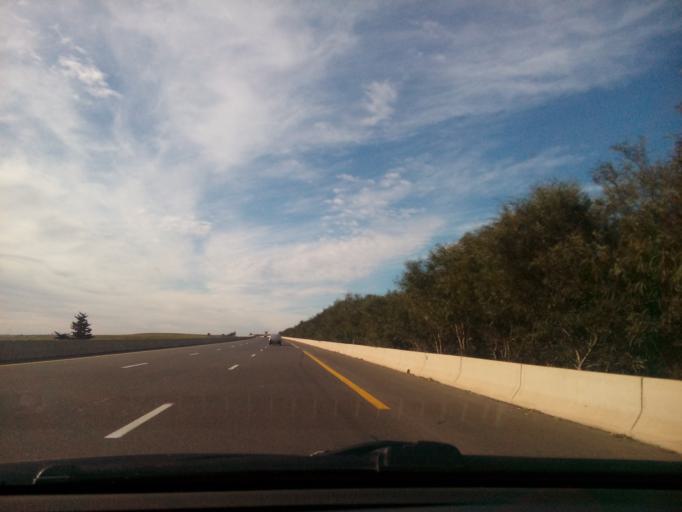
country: DZ
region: Sidi Bel Abbes
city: Sidi Bel Abbes
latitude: 35.1722
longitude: -0.7593
